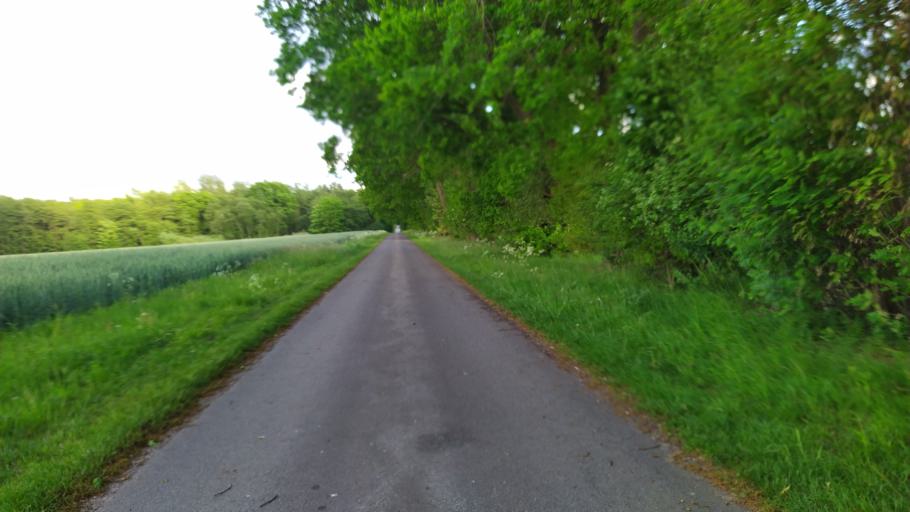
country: DE
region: Lower Saxony
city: Bargstedt
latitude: 53.4751
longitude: 9.4599
